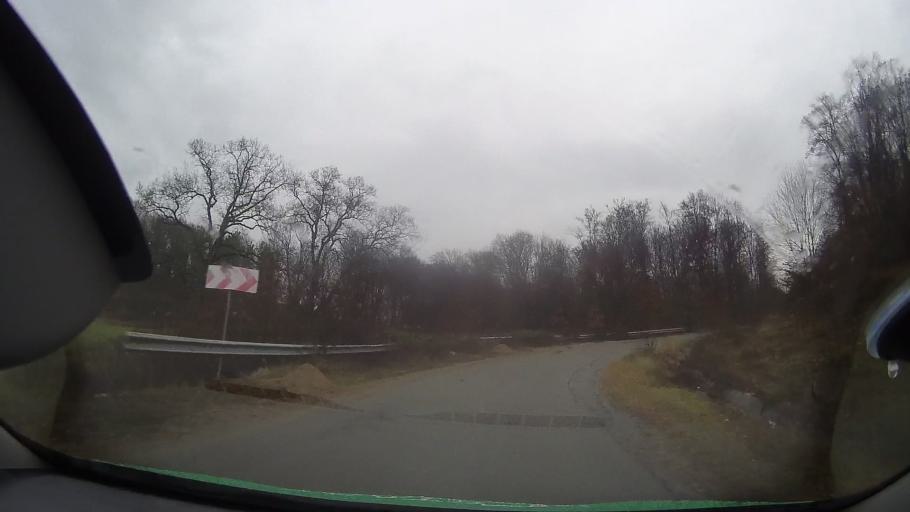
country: RO
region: Bihor
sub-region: Comuna Rabagani
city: Rabagani
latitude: 46.7233
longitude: 22.2334
